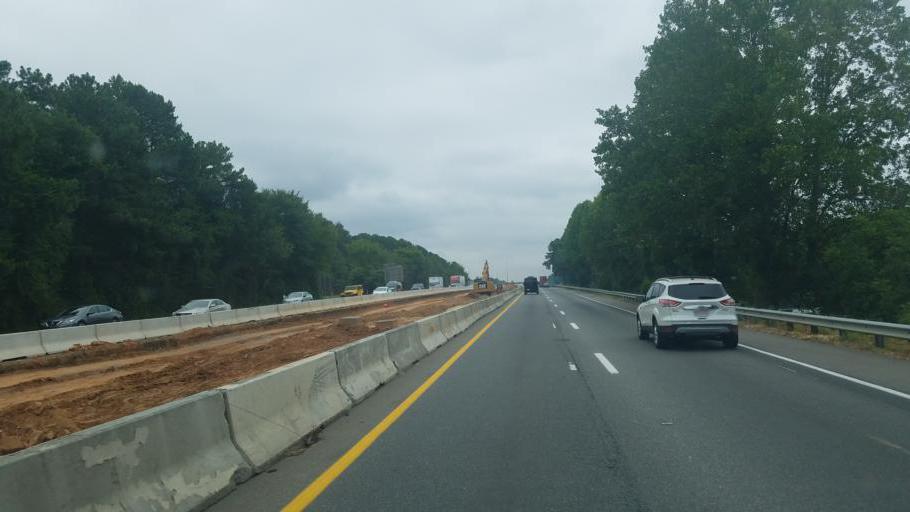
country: US
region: North Carolina
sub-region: Gaston County
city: Davidson
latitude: 35.5189
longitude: -80.8648
